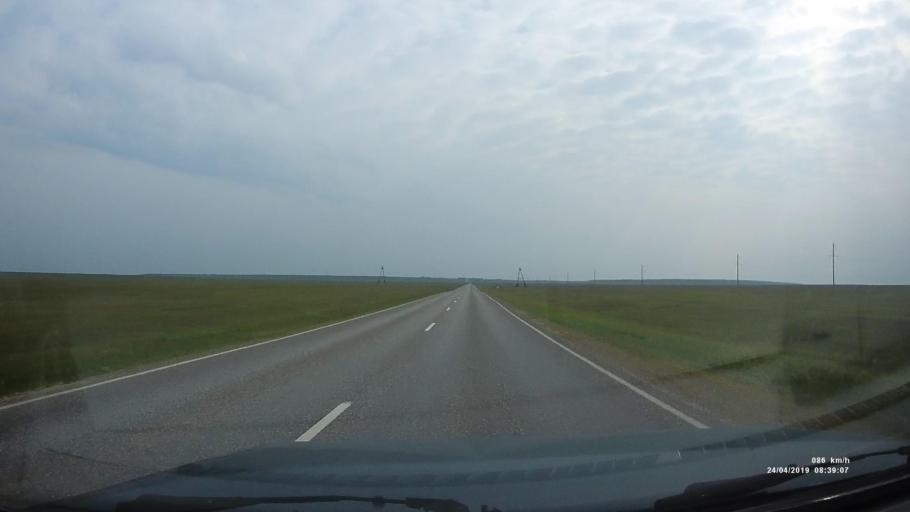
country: RU
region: Kalmykiya
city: Arshan'
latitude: 46.2191
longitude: 43.9787
